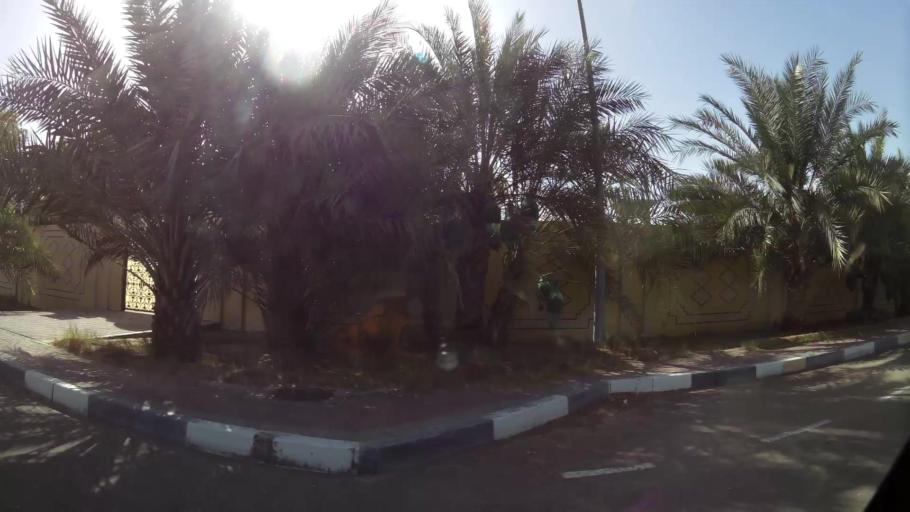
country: OM
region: Al Buraimi
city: Al Buraymi
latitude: 24.3267
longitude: 55.7965
